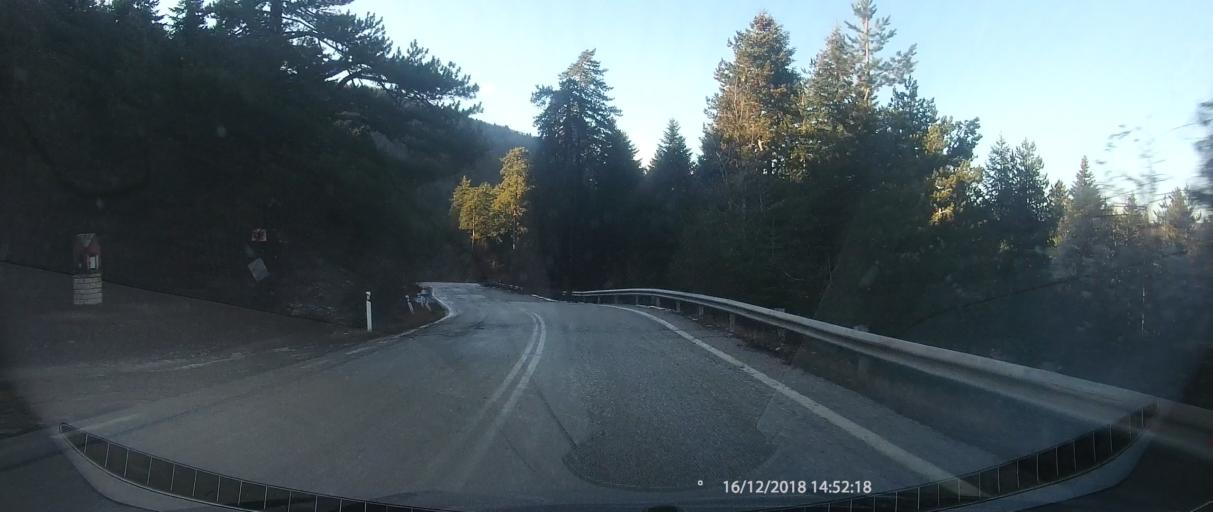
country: GR
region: West Macedonia
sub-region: Nomos Kastorias
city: Nestorio
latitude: 40.2048
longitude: 21.0636
